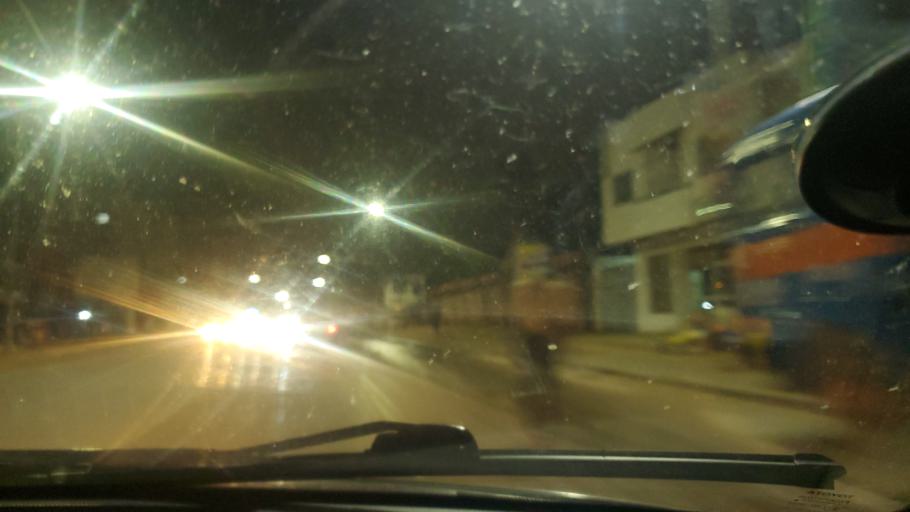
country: SN
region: Dakar
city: Grand Dakar
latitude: 14.7240
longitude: -17.4458
